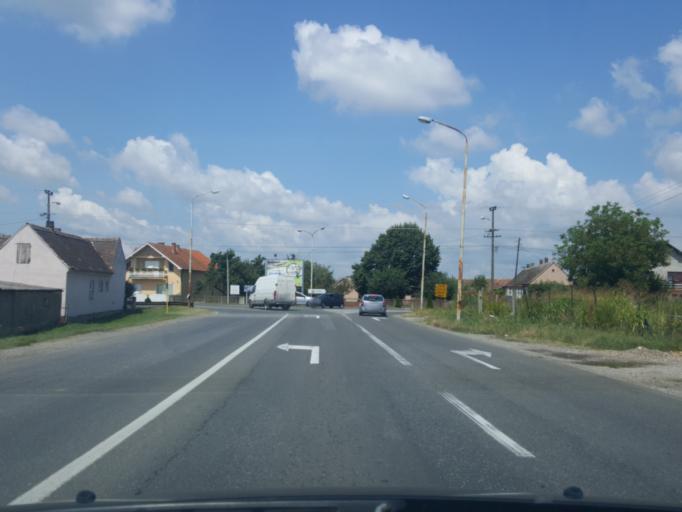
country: RS
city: Macvanska Mitrovica
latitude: 44.9561
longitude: 19.6009
